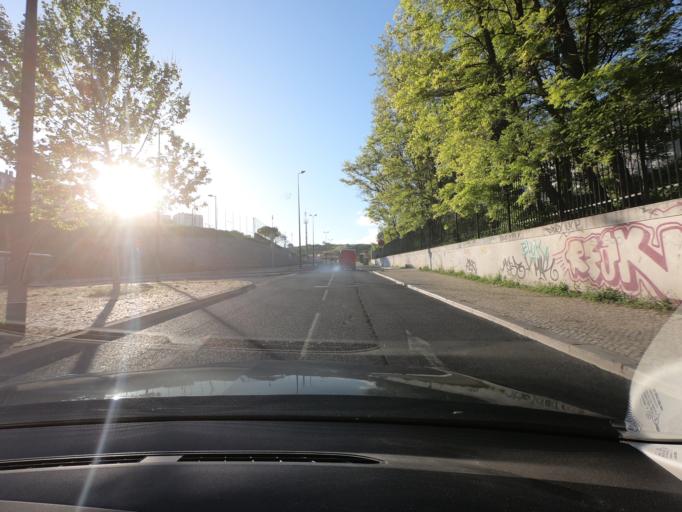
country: PT
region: Lisbon
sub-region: Lisbon
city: Lisbon
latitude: 38.7214
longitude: -9.1194
